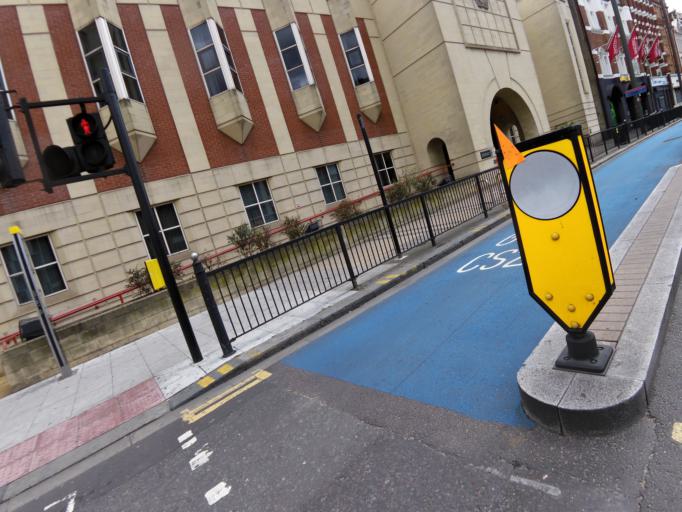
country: GB
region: England
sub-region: Greater London
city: Poplar
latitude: 51.5394
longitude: 0.0000
